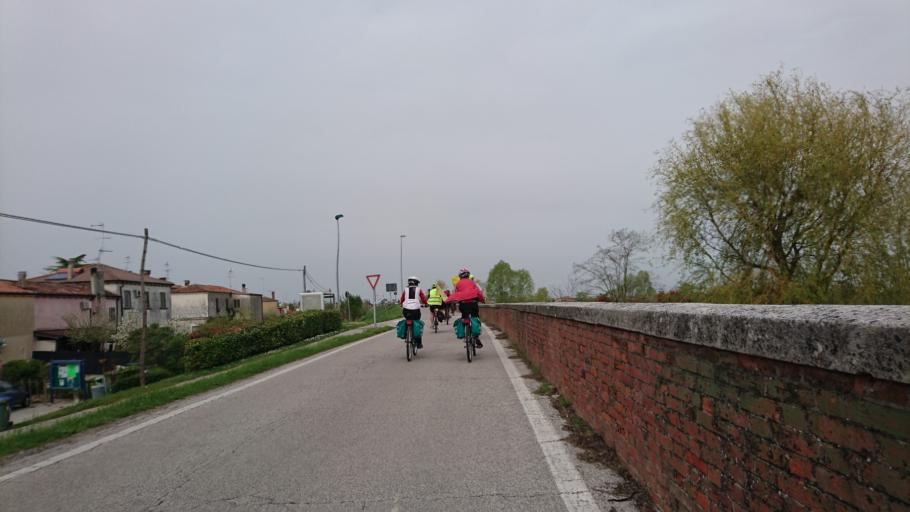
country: IT
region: Veneto
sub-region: Provincia di Venezia
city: La Salute di Livenza
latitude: 45.6480
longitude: 12.8144
